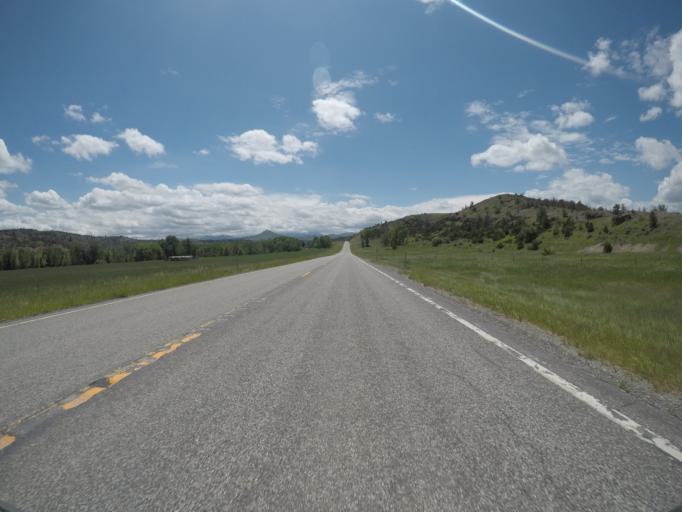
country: US
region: Montana
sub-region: Sweet Grass County
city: Big Timber
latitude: 45.7447
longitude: -109.9956
